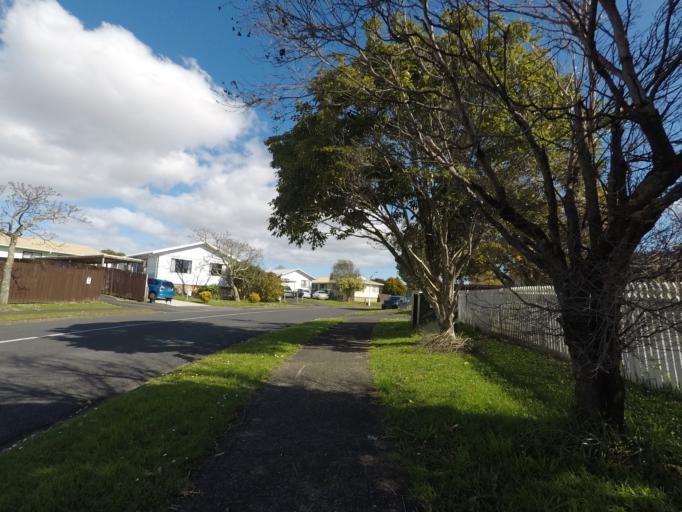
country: NZ
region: Auckland
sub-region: Auckland
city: Rosebank
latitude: -36.8612
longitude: 174.6020
